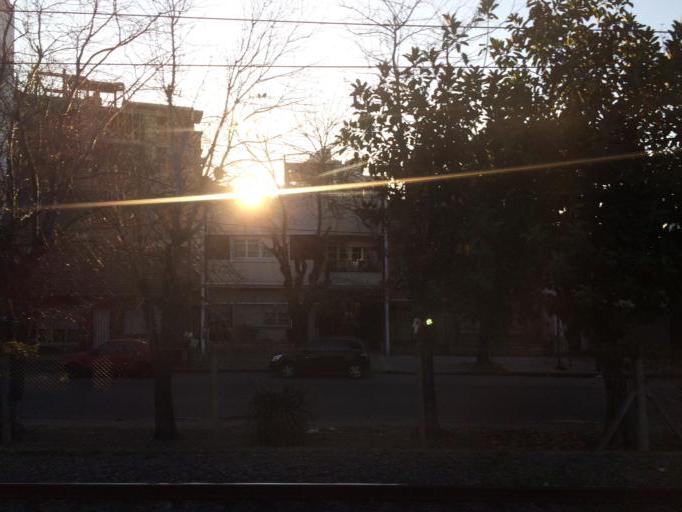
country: AR
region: Buenos Aires
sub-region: Partido de Lanus
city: Lanus
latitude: -34.7023
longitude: -58.3886
